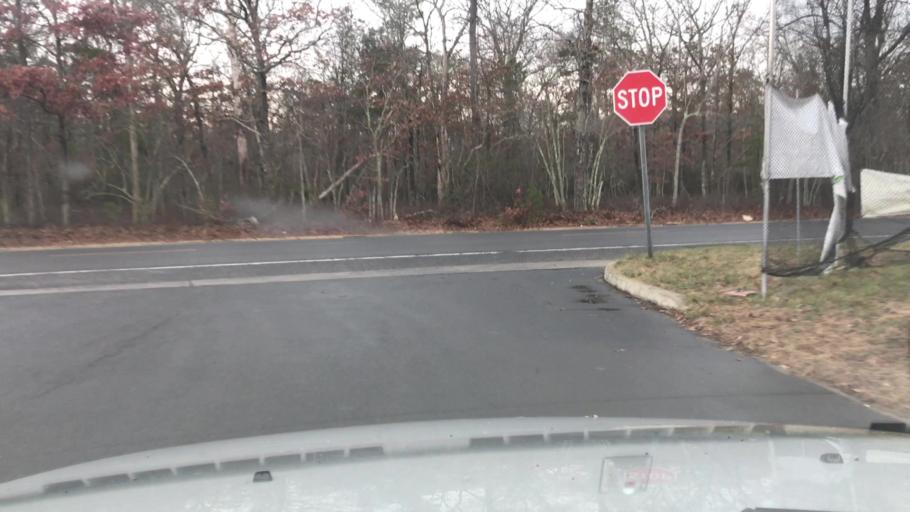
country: US
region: New Jersey
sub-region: Cape May County
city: Sea Isle City
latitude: 39.1976
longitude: -74.7497
